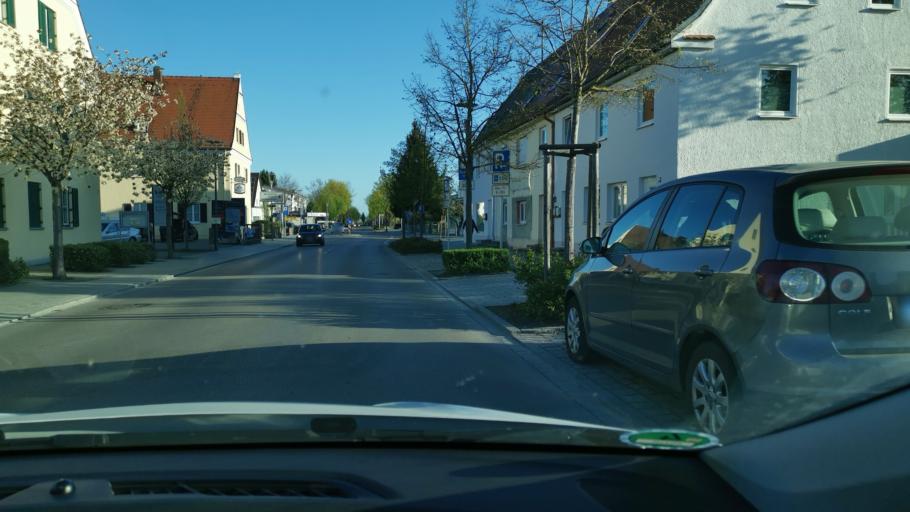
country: DE
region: Bavaria
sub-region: Swabia
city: Meitingen
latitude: 48.5482
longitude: 10.8533
